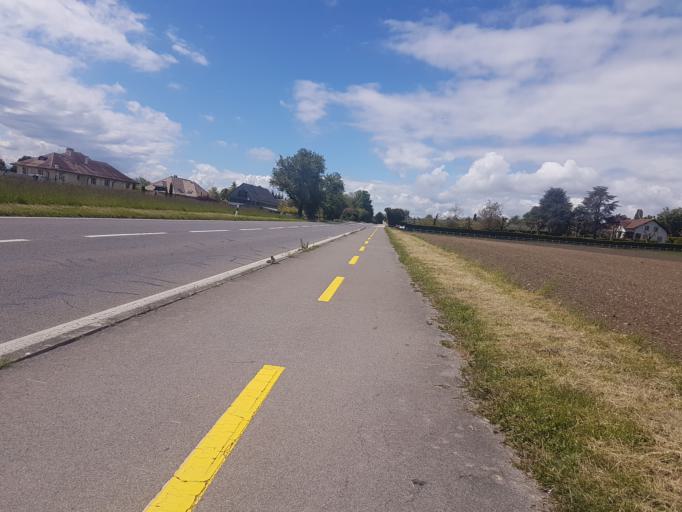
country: CH
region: Vaud
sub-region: Nyon District
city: Gland
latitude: 46.4313
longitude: 6.3027
